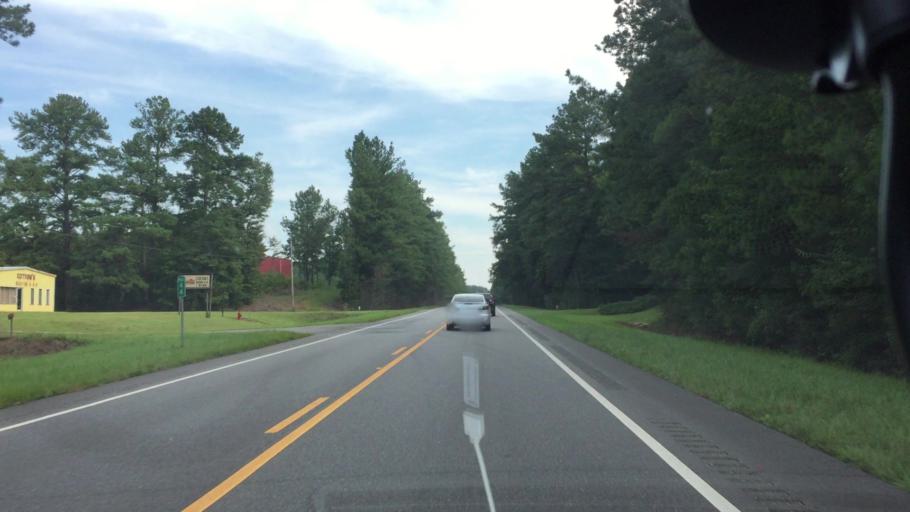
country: US
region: Alabama
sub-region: Coffee County
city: New Brockton
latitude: 31.5614
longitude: -85.9241
